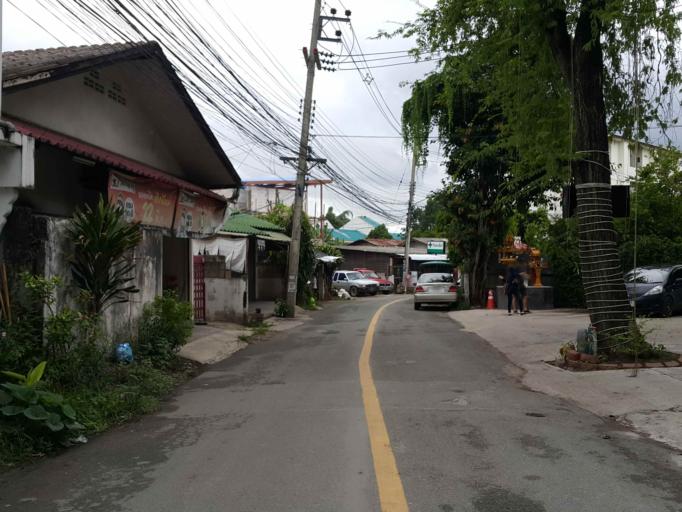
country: TH
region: Chiang Mai
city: Chiang Mai
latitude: 18.8162
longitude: 98.9977
